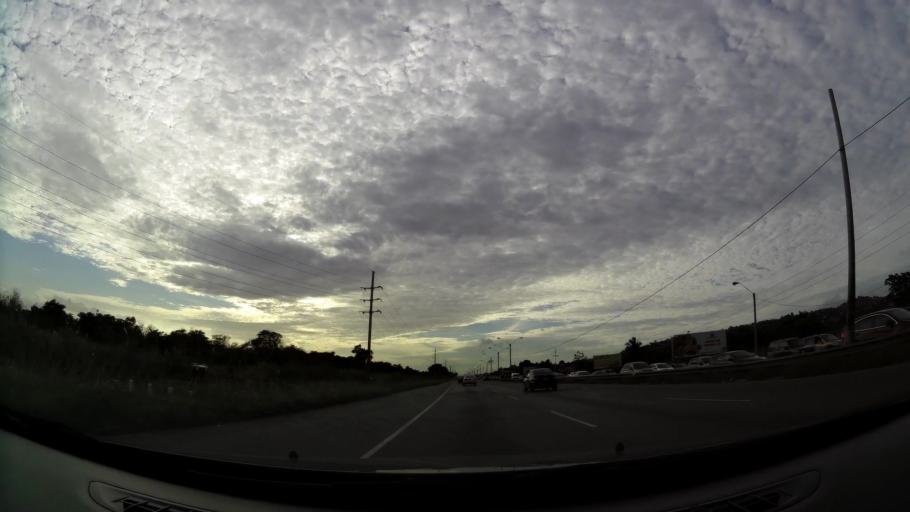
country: TT
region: San Juan/Laventille
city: Laventille
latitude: 10.6446
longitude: -61.4757
